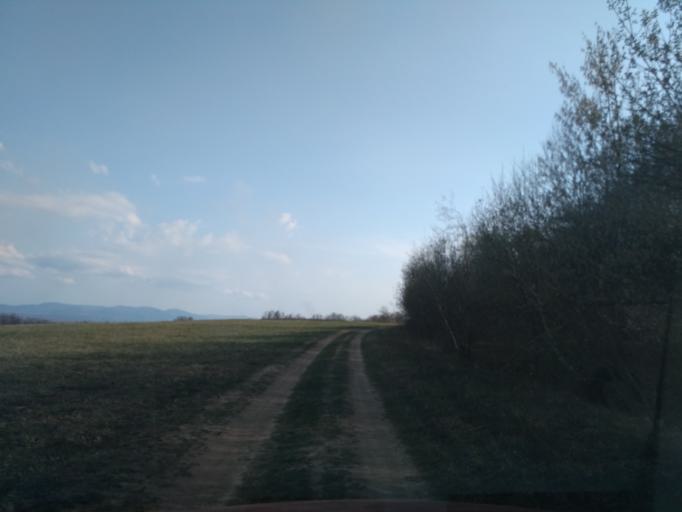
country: SK
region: Kosicky
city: Kosice
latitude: 48.6801
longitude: 21.1814
